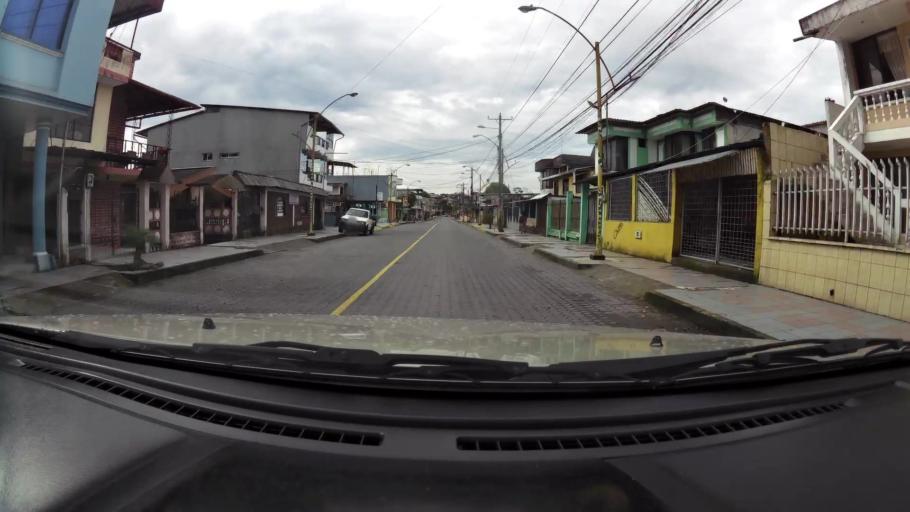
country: EC
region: Pastaza
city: Puyo
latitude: -1.4808
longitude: -77.9985
